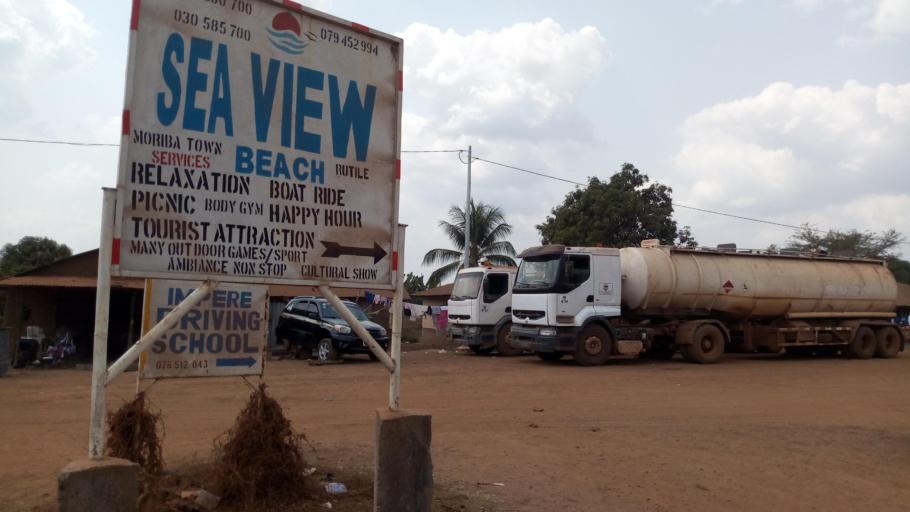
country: SL
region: Southern Province
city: Mogbwemo
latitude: 7.7882
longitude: -12.3061
